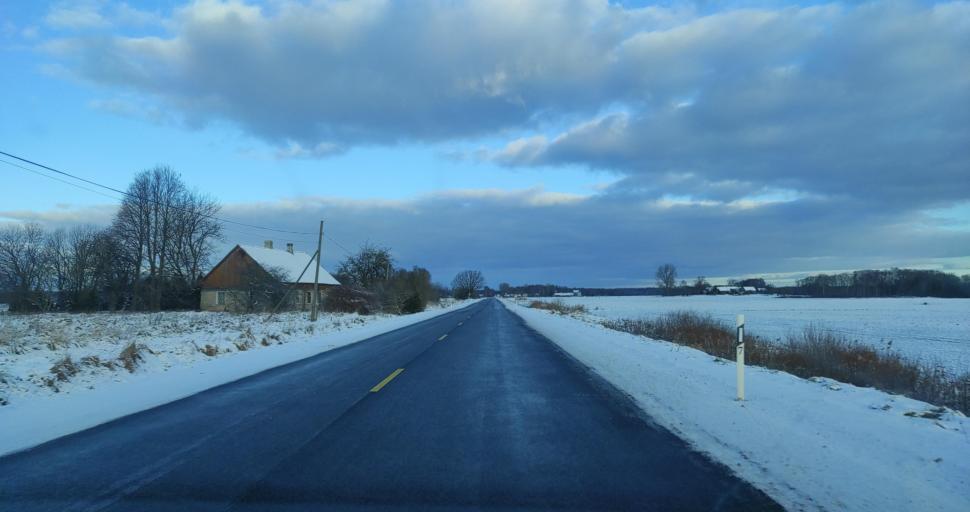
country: LV
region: Skrunda
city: Skrunda
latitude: 56.6976
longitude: 22.0189
